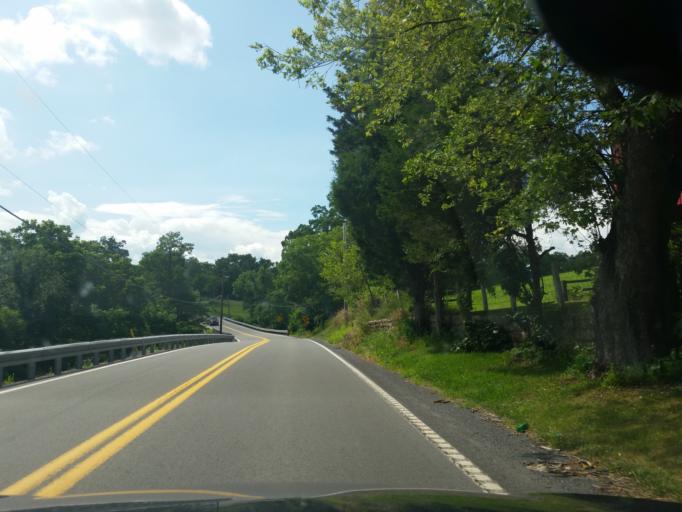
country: US
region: Pennsylvania
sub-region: Dauphin County
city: Elizabethville
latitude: 40.5143
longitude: -76.8584
